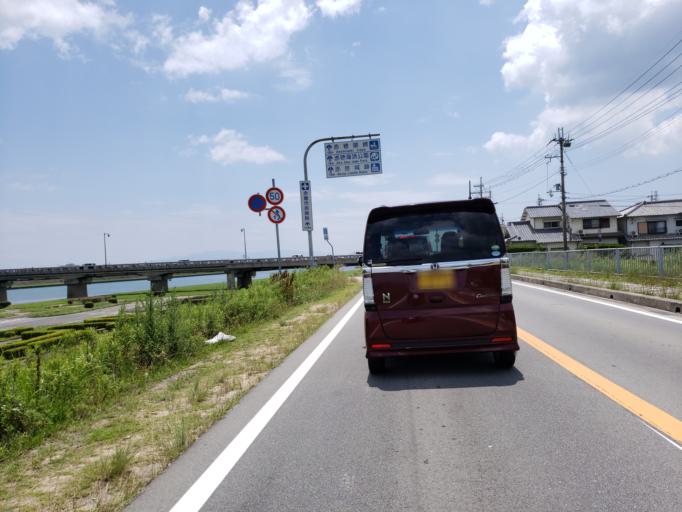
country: JP
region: Hyogo
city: Kariya
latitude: 34.7503
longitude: 134.3992
